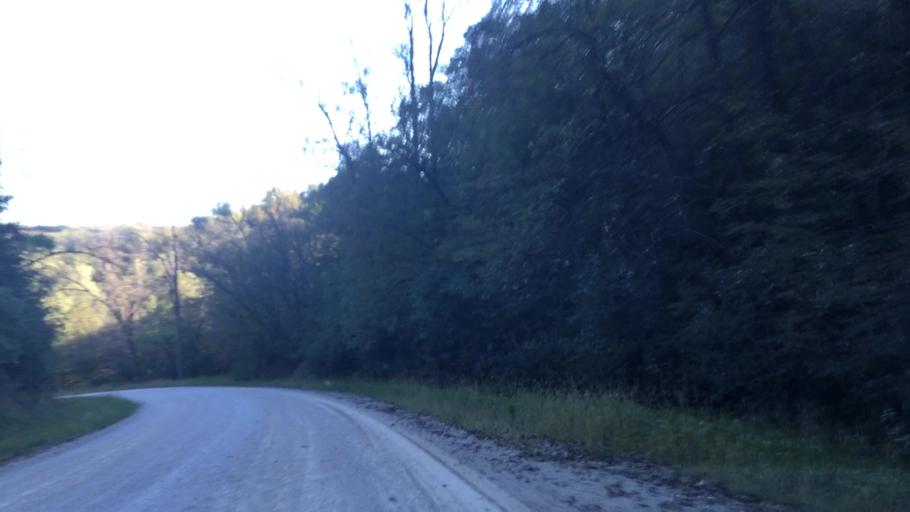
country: US
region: Minnesota
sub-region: Fillmore County
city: Preston
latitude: 43.7643
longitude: -92.0296
